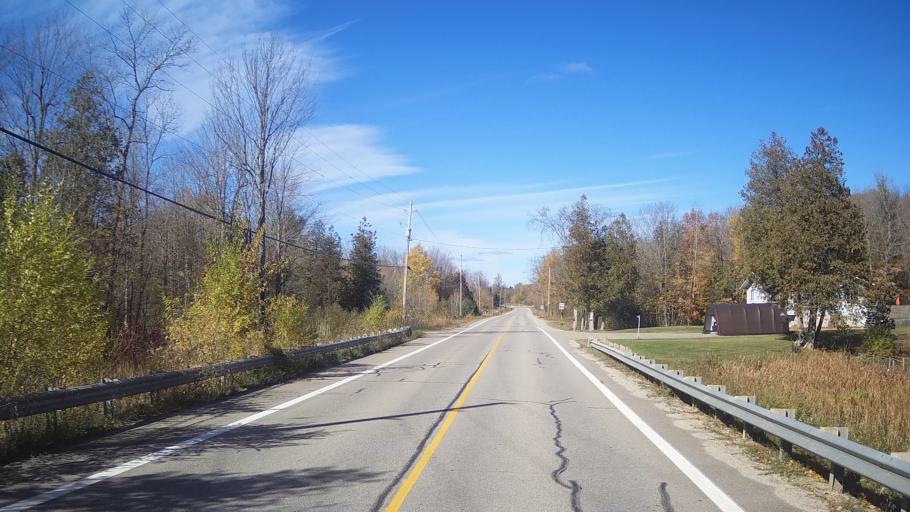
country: CA
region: Ontario
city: Perth
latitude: 44.8697
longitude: -76.2920
